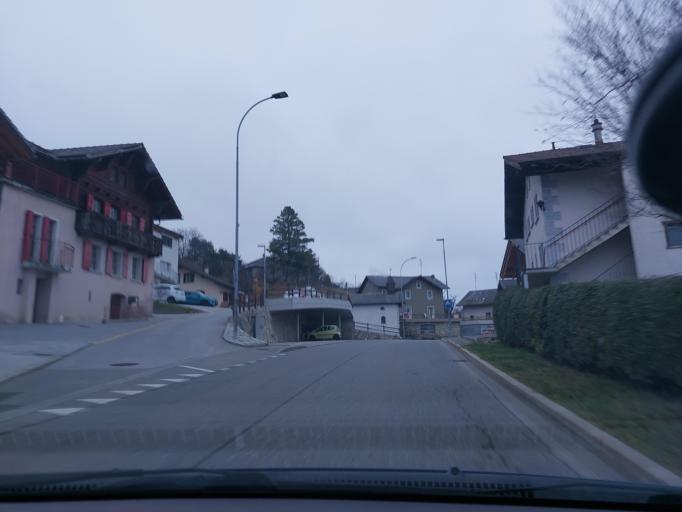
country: CH
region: Valais
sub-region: Herens District
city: Ayent
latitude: 46.2758
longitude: 7.4039
